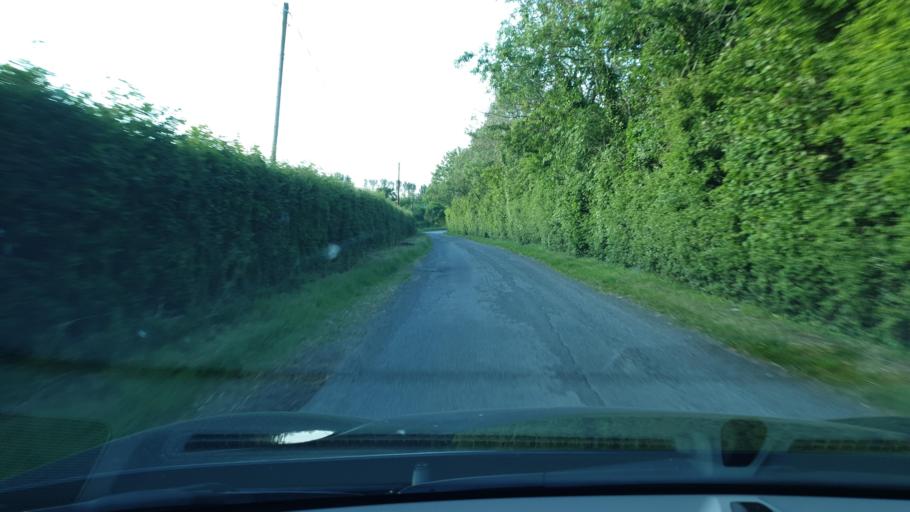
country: IE
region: Leinster
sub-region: Fingal County
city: Blanchardstown
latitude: 53.4391
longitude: -6.3959
